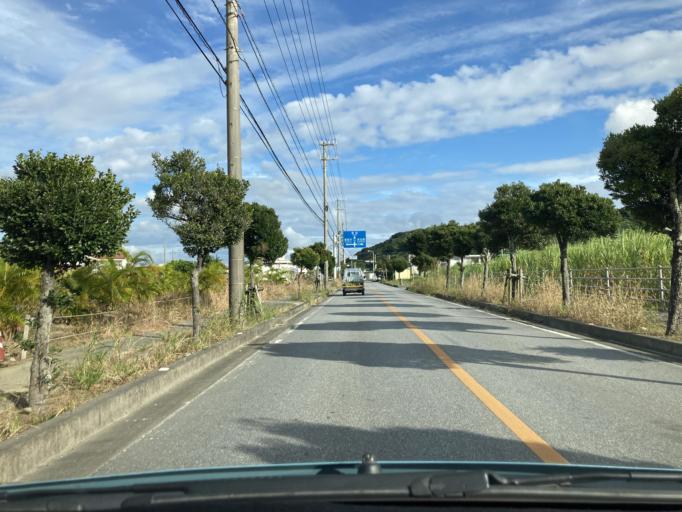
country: JP
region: Okinawa
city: Itoman
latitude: 26.1351
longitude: 127.7084
